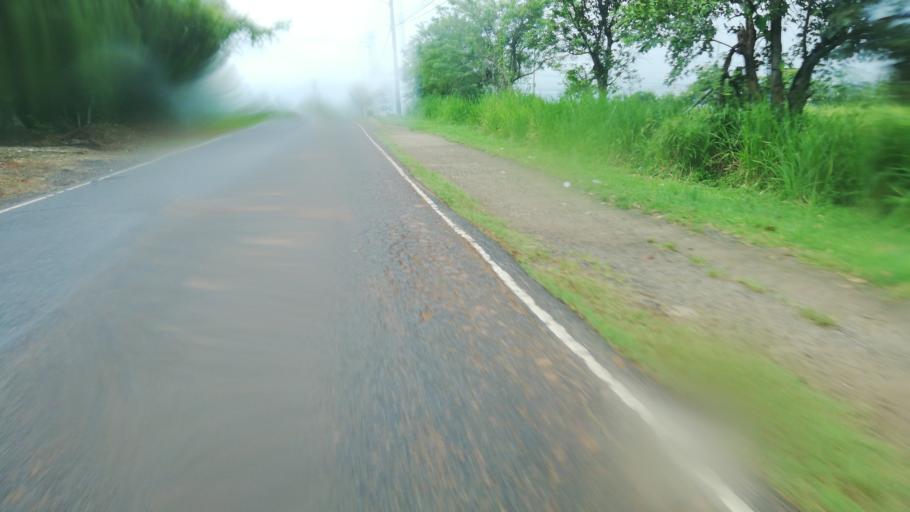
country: PA
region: Panama
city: Pacora
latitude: 9.0966
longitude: -79.2885
